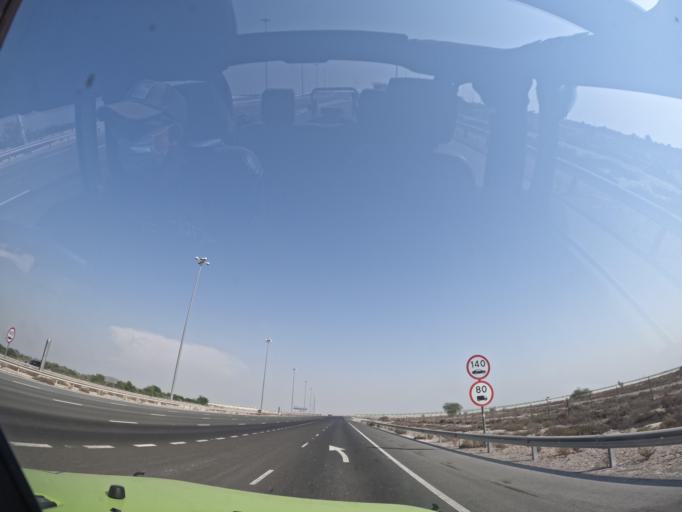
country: AE
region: Abu Dhabi
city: Abu Dhabi
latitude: 24.6906
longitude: 54.7848
